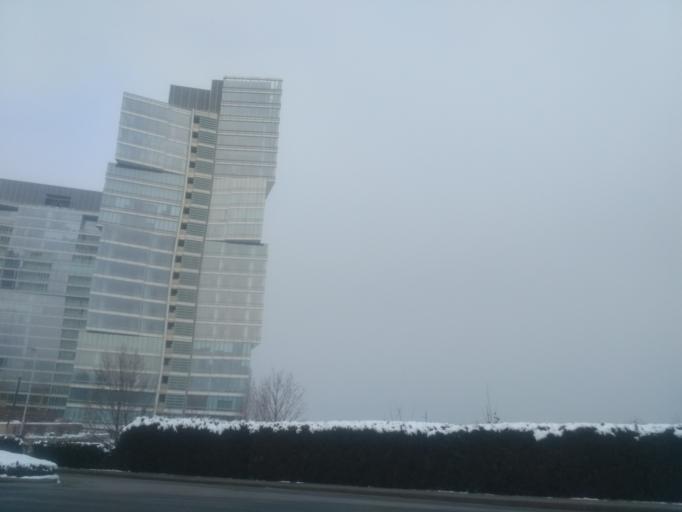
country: KZ
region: Almaty Qalasy
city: Almaty
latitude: 43.2194
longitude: 76.9310
